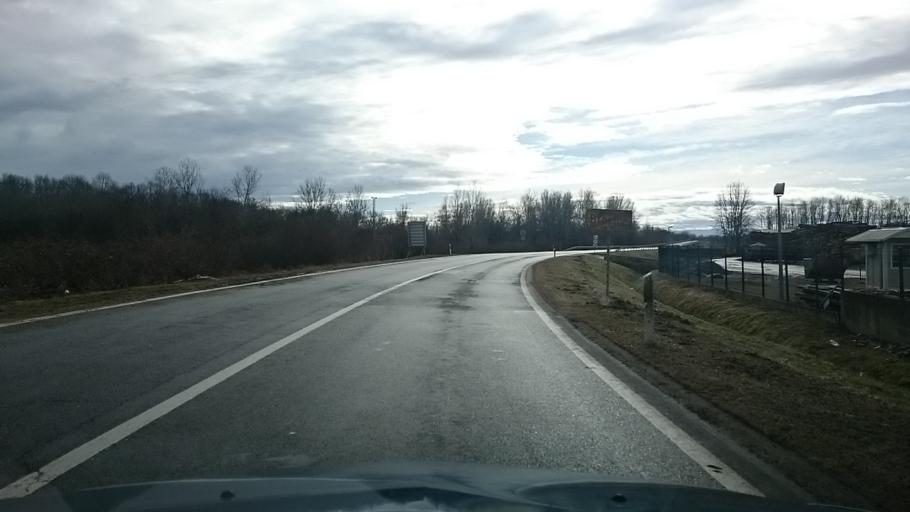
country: HR
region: Sisacko-Moslavacka
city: Novska
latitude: 45.3014
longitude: 16.9518
